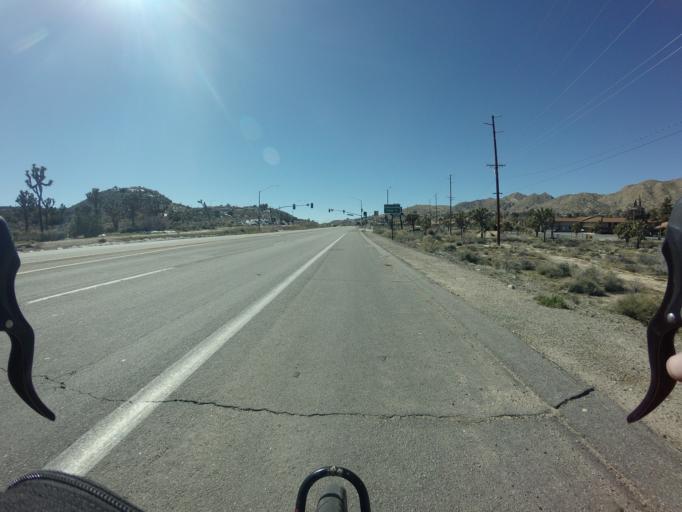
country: US
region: California
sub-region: San Bernardino County
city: Yucca Valley
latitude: 34.1145
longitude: -116.4657
